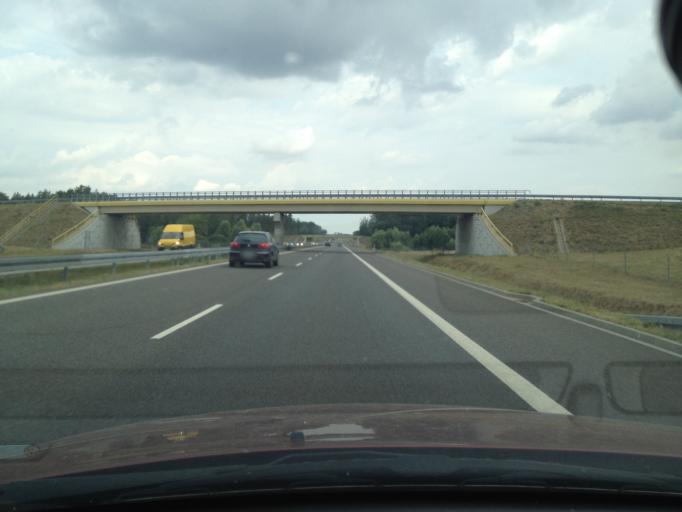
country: PL
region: West Pomeranian Voivodeship
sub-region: Powiat mysliborski
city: Mysliborz
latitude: 53.0064
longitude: 14.8619
